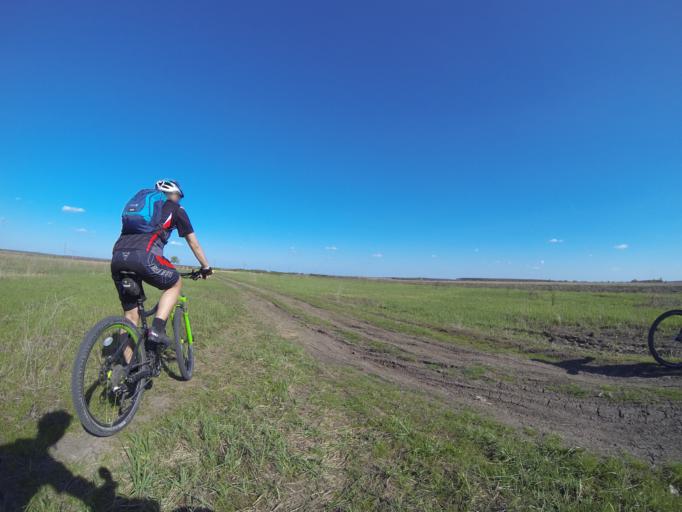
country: RO
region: Dolj
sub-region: Comuna Goesti
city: Goesti
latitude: 44.5091
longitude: 23.7919
